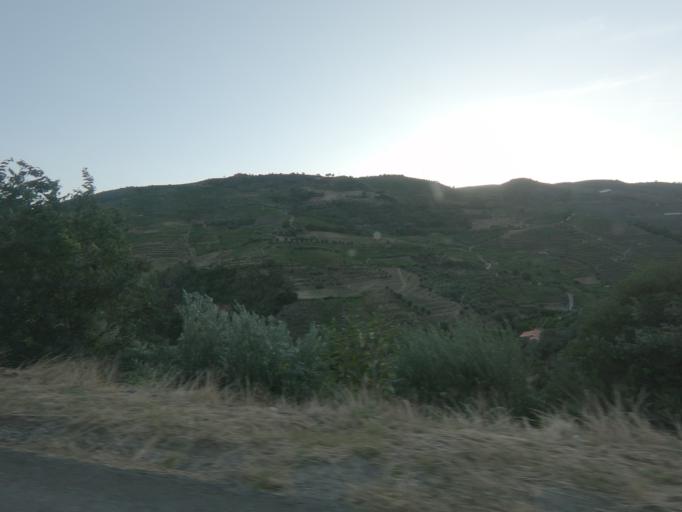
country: PT
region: Viseu
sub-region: Armamar
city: Armamar
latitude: 41.1613
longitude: -7.6839
